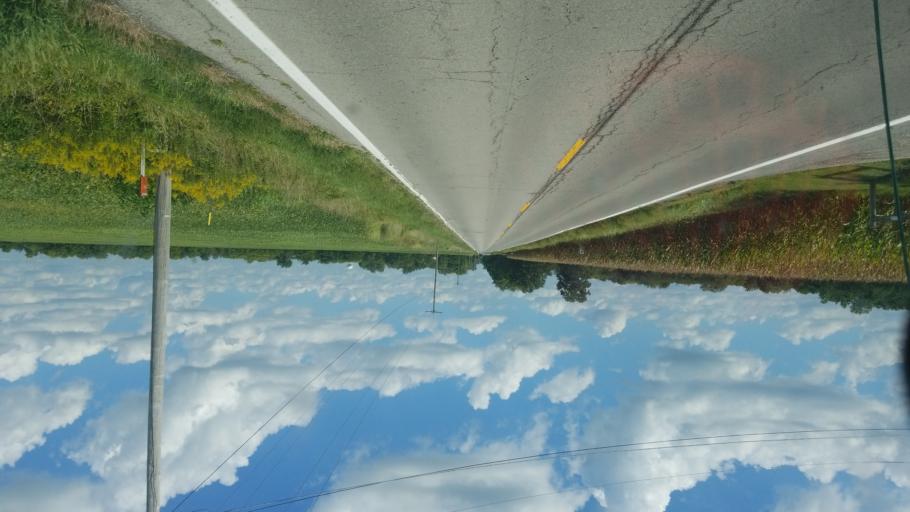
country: US
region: Ohio
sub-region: Union County
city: Richwood
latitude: 40.4089
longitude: -83.2878
